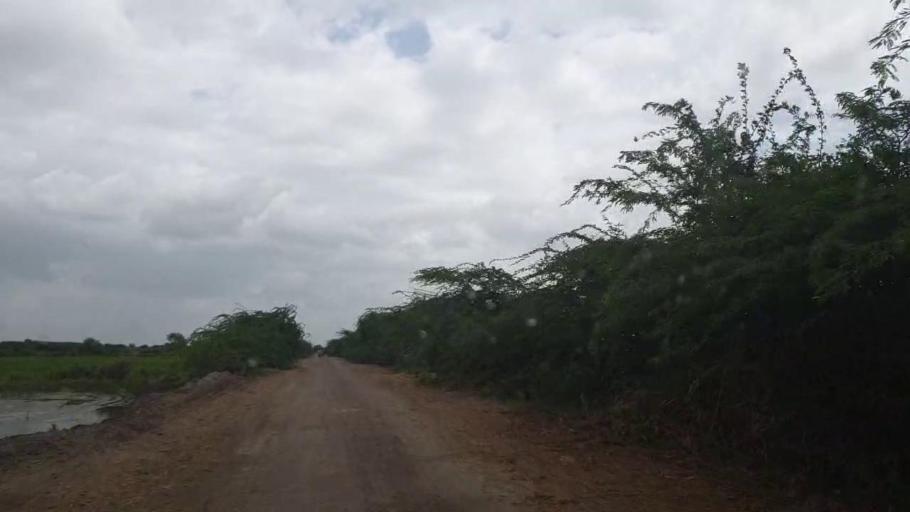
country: PK
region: Sindh
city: Badin
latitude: 24.6455
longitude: 68.9458
